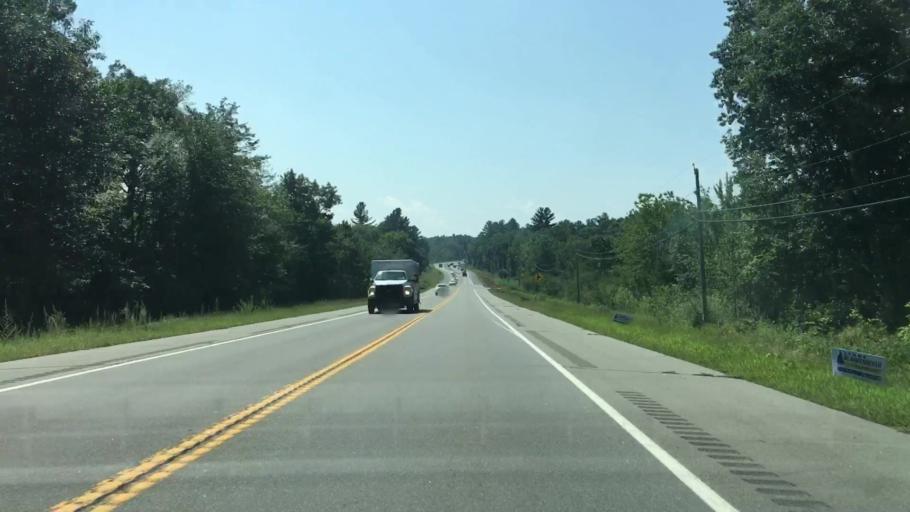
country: US
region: New Hampshire
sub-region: Rockingham County
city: Hampstead
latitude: 42.8417
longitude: -71.2270
